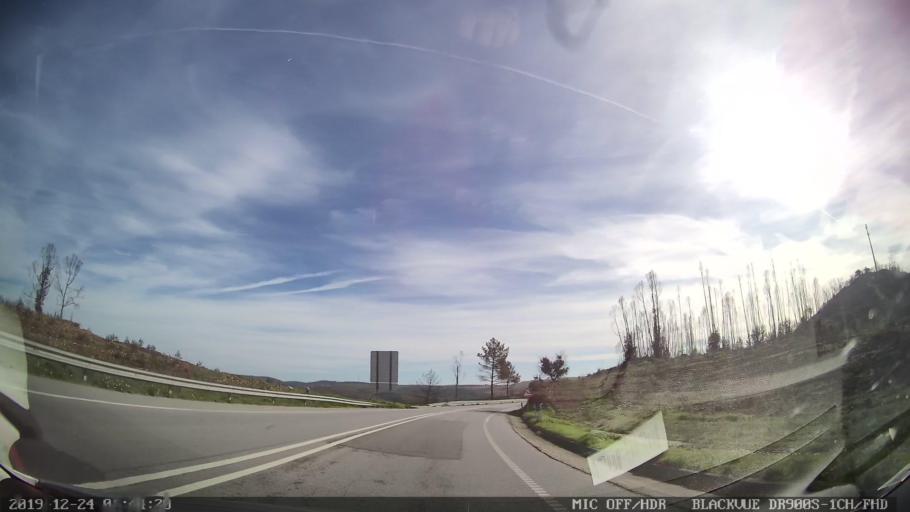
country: PT
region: Portalegre
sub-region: Nisa
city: Nisa
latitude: 39.5559
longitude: -7.7948
